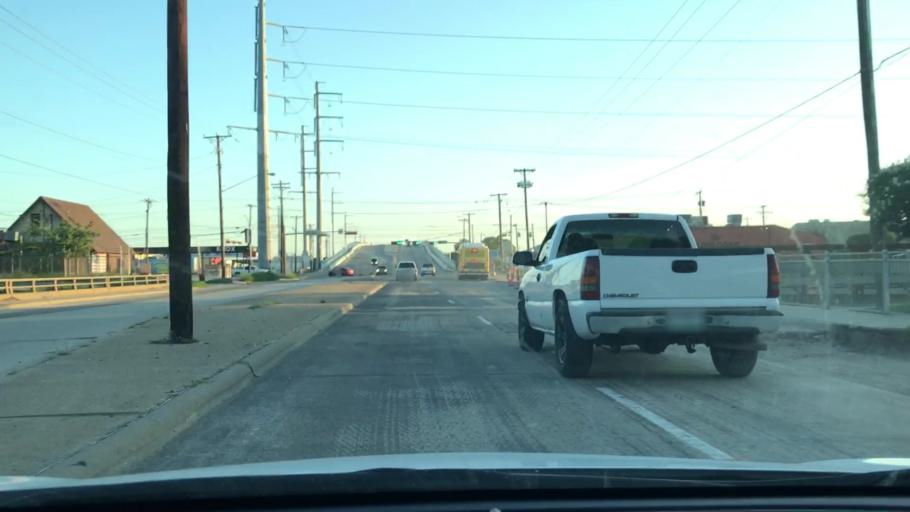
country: US
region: Texas
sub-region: Dallas County
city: Dallas
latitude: 32.7972
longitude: -96.8336
